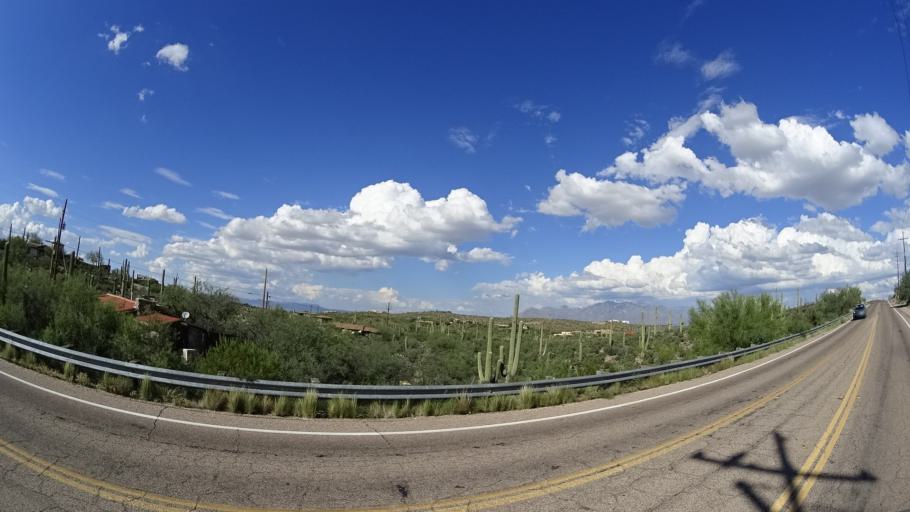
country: US
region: Arizona
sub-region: Pima County
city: Tucson Estates
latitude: 32.2359
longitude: -111.0579
